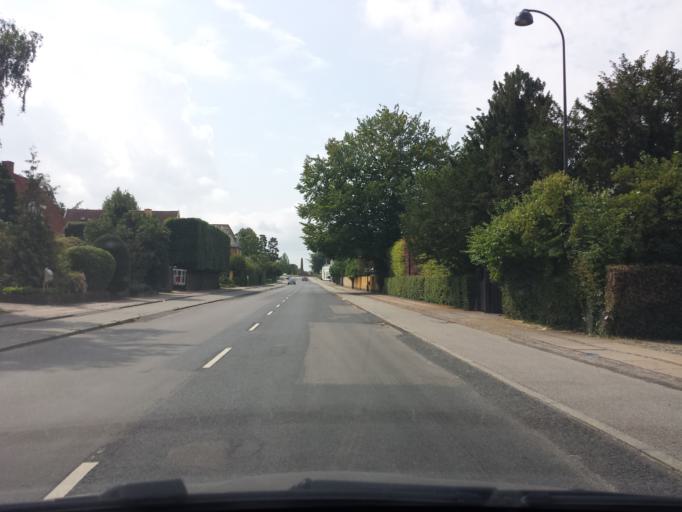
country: DK
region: Capital Region
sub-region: Gentofte Kommune
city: Charlottenlund
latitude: 55.7608
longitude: 12.5584
